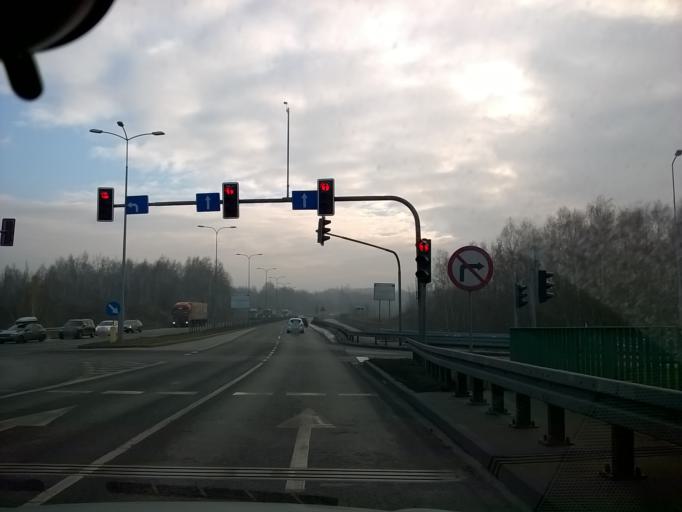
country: PL
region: Silesian Voivodeship
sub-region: Ruda Slaska
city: Ruda Slaska
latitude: 50.2987
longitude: 18.8584
